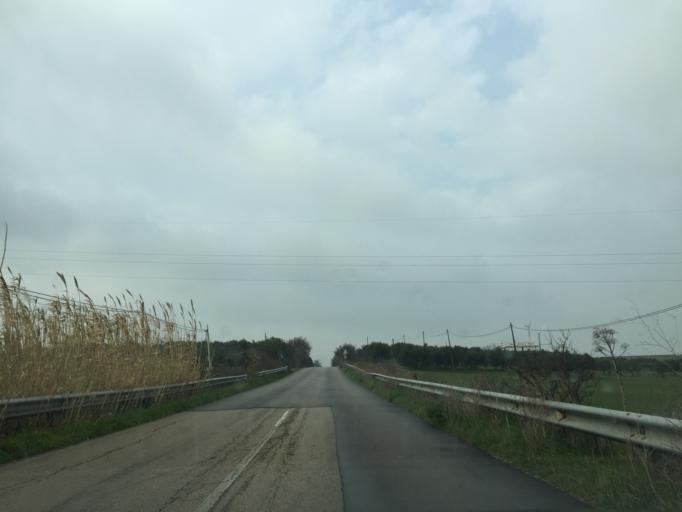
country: IT
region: Apulia
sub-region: Provincia di Foggia
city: Troia
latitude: 41.3836
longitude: 15.3815
